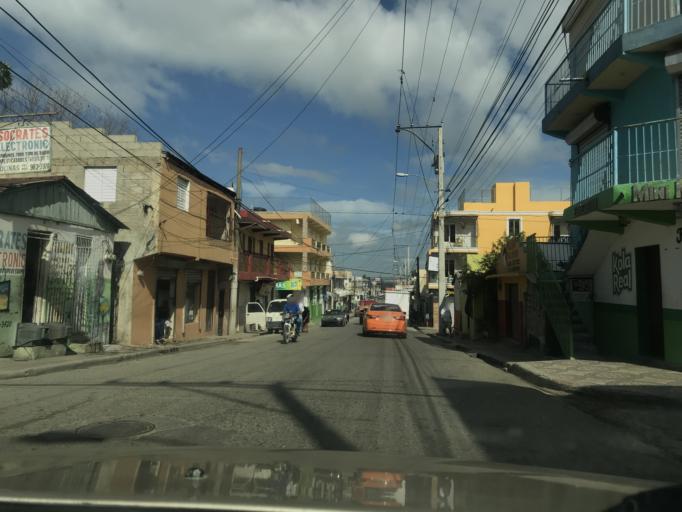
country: DO
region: Santiago
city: Palmar Arriba
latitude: 19.4851
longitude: -70.7440
